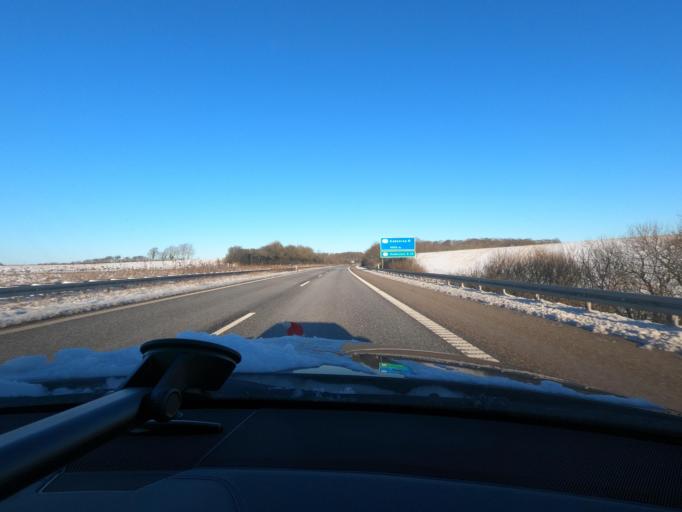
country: DK
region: South Denmark
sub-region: Aabenraa Kommune
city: Rodekro
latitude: 55.0521
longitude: 9.3533
